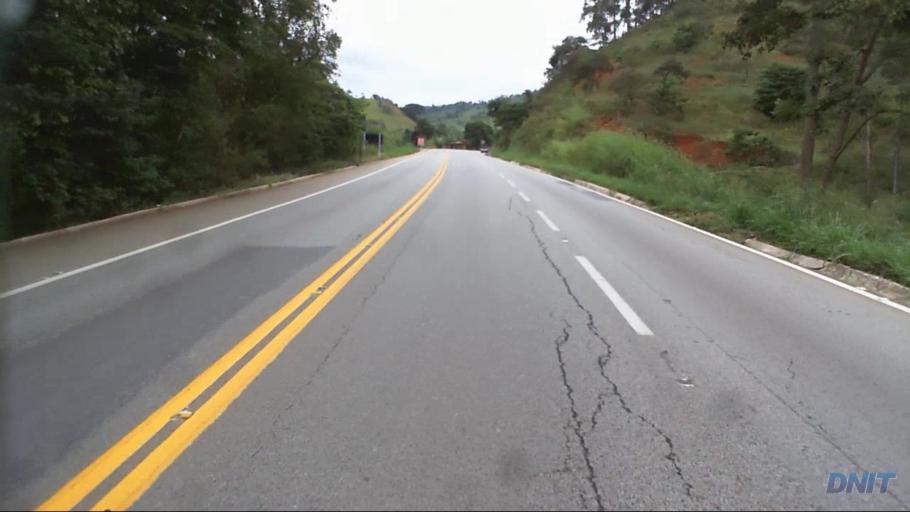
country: BR
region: Minas Gerais
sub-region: Nova Era
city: Nova Era
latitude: -19.7801
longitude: -43.0437
